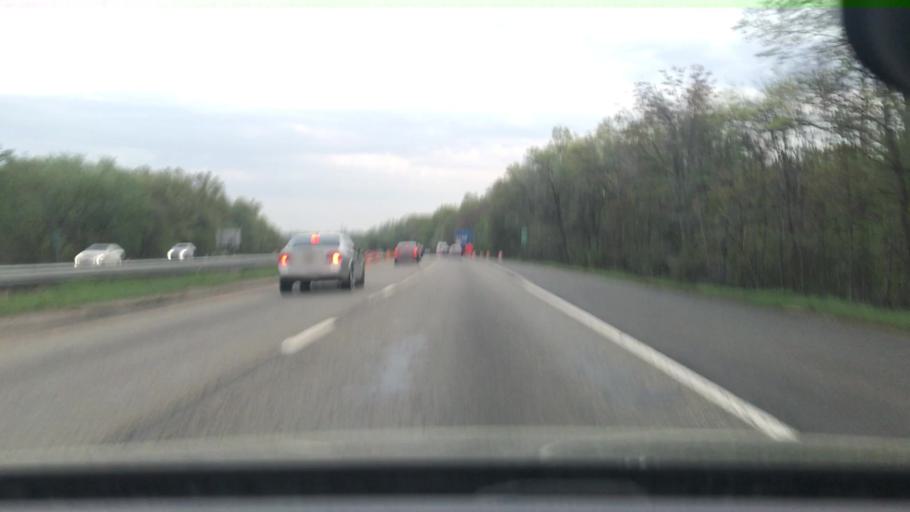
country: US
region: New Jersey
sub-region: Essex County
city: West Caldwell
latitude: 40.8339
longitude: -74.3344
